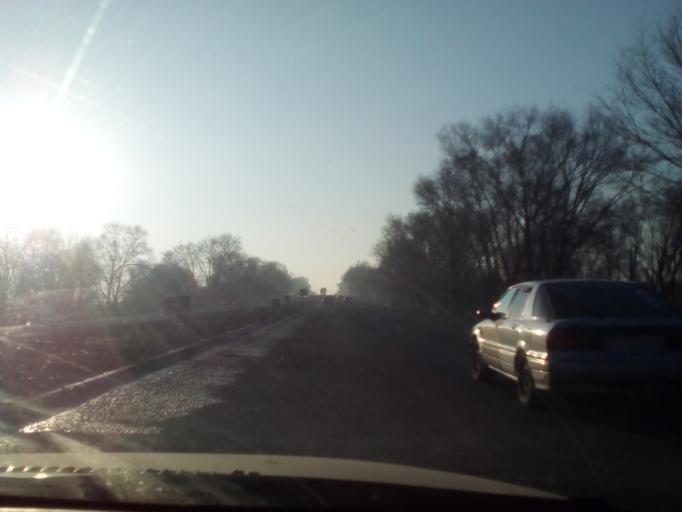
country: KZ
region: Almaty Oblysy
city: Burunday
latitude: 43.2228
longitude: 76.5820
